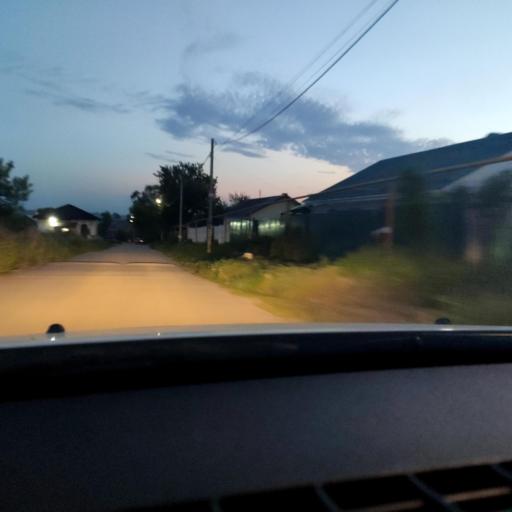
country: RU
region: Voronezj
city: Podgornoye
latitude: 51.8003
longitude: 39.1404
